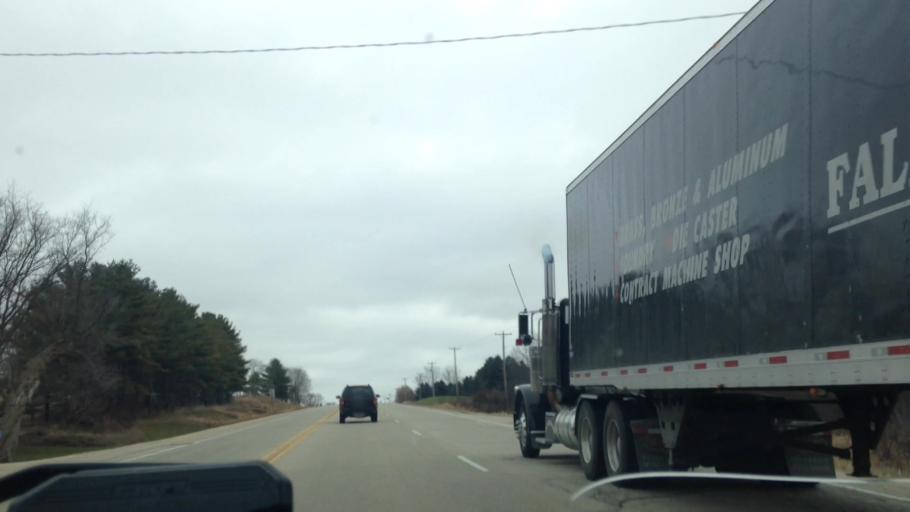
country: US
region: Wisconsin
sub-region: Dodge County
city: Mayville
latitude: 43.4428
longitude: -88.5370
